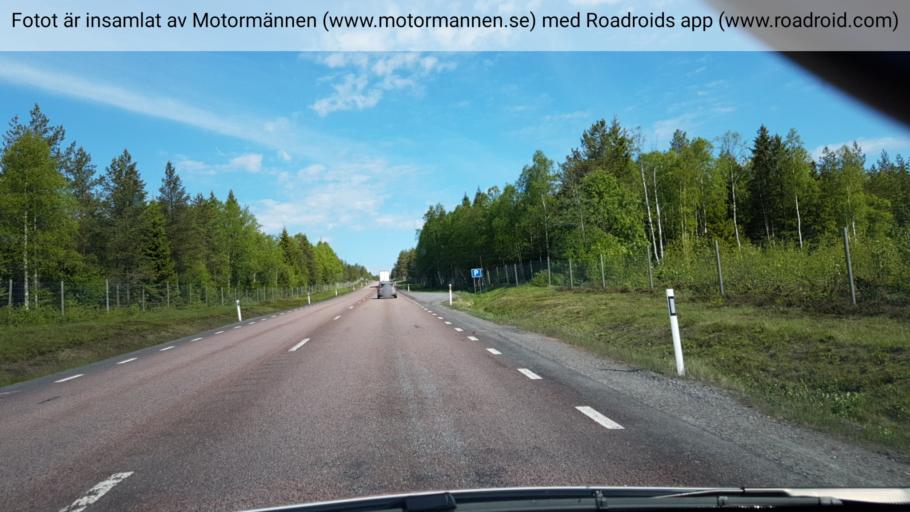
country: SE
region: Vaesterbotten
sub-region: Skelleftea Kommun
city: Burea
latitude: 64.4249
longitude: 21.2846
